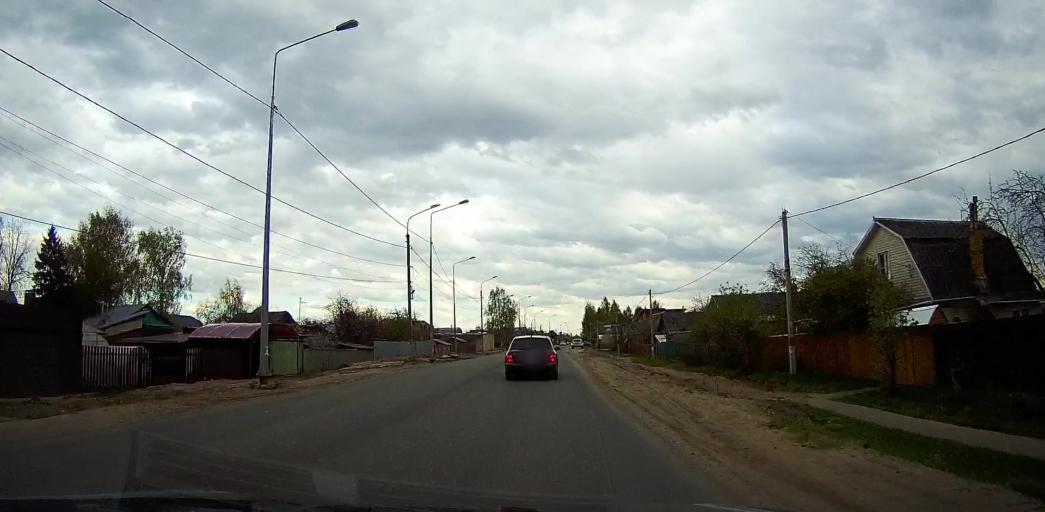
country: RU
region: Moskovskaya
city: Pavlovskiy Posad
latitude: 55.7696
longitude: 38.6944
